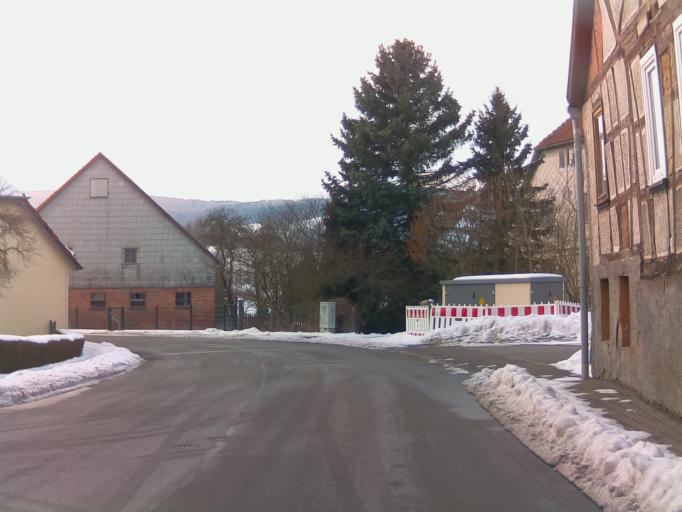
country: DE
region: Thuringia
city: Erbenhausen
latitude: 50.5759
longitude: 10.1451
